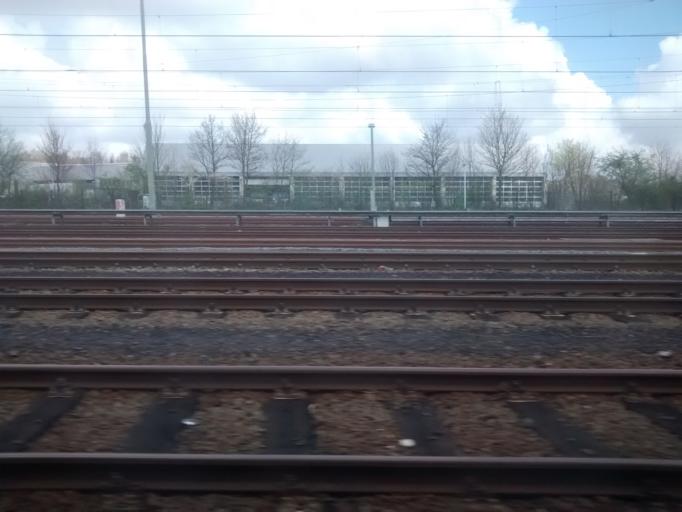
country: NL
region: Limburg
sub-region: Gemeente Heerlen
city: Heerlen
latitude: 50.8930
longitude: 5.9654
